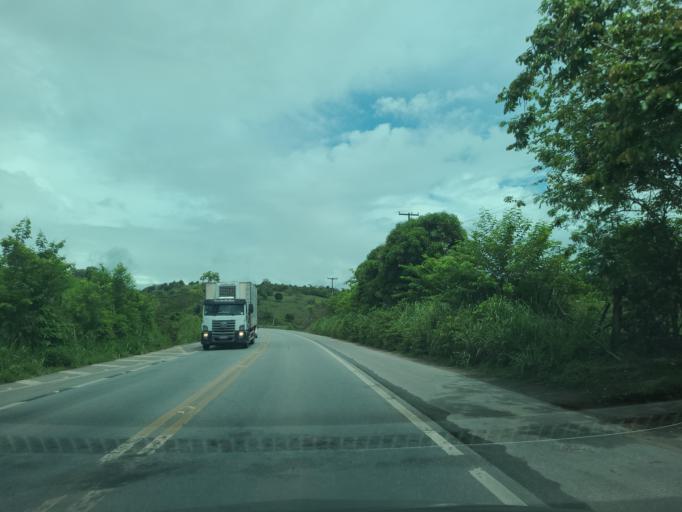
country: BR
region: Alagoas
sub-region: Uniao Dos Palmares
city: Uniao dos Palmares
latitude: -9.2188
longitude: -36.0324
